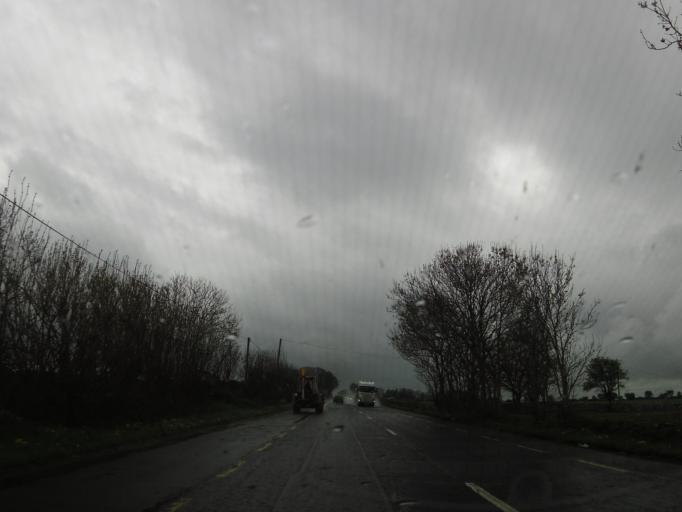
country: IE
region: Connaught
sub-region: County Galway
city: Claregalway
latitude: 53.3854
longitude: -8.9168
